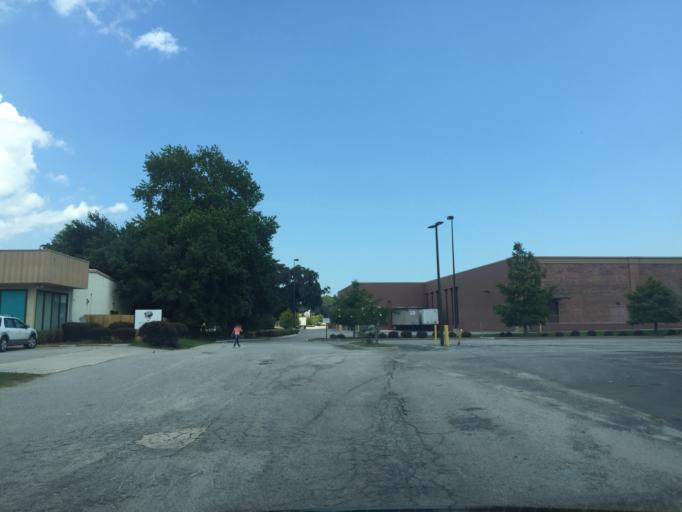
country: US
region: Georgia
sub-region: Chatham County
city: Isle of Hope
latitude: 32.0075
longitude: -81.1141
